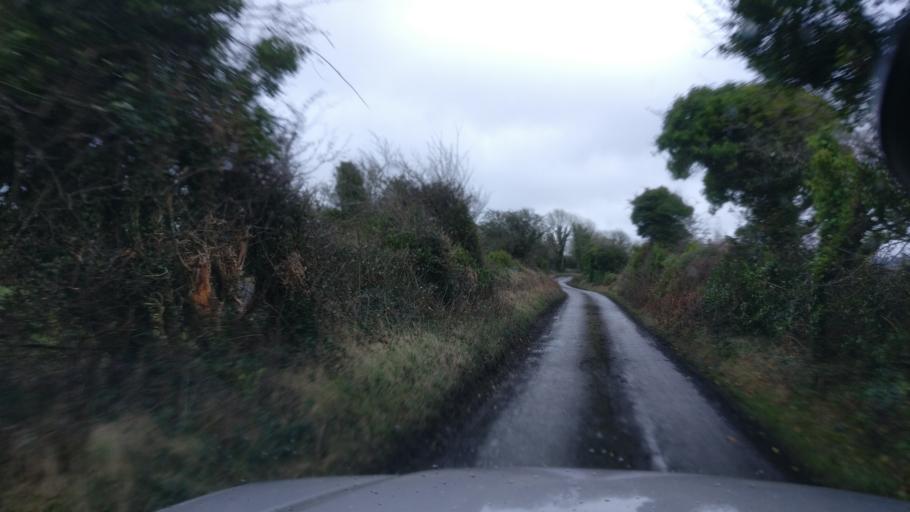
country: IE
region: Connaught
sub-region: County Galway
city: Loughrea
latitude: 53.2011
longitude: -8.6678
